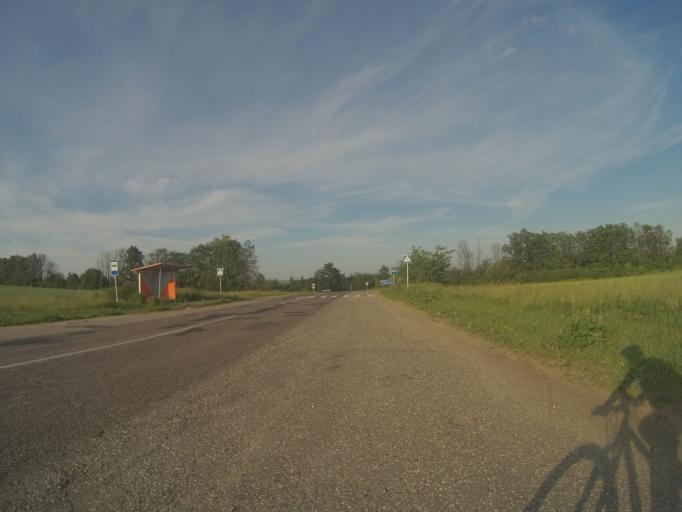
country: RU
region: Vladimir
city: Suzdal'
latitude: 56.3757
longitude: 40.4578
